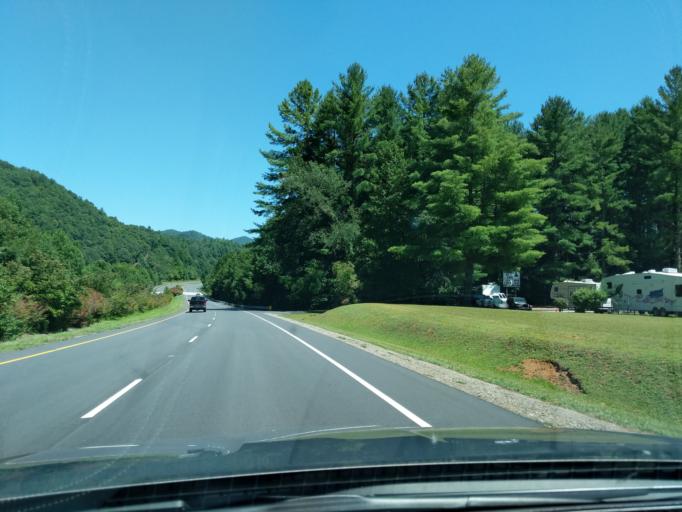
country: US
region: North Carolina
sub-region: Macon County
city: Franklin
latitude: 35.1493
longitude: -83.4674
